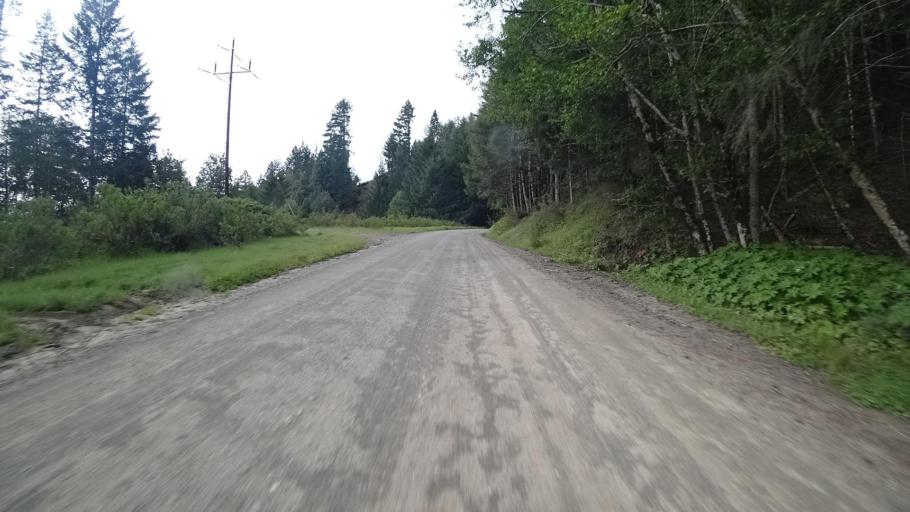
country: US
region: California
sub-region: Humboldt County
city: Redway
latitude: 40.2642
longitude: -123.7696
